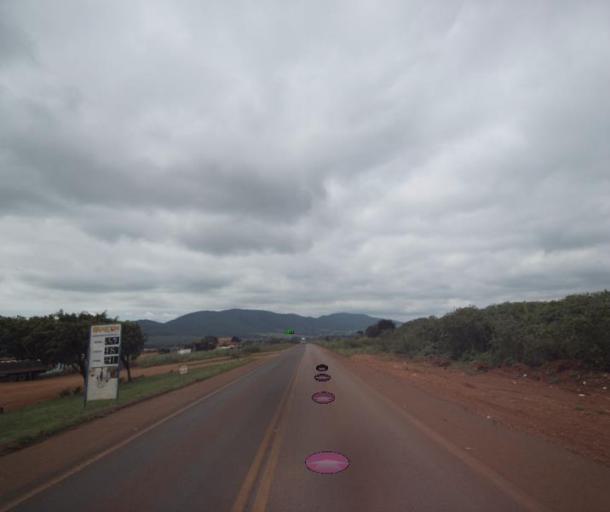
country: BR
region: Goias
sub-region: Barro Alto
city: Barro Alto
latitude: -14.9680
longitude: -48.9308
